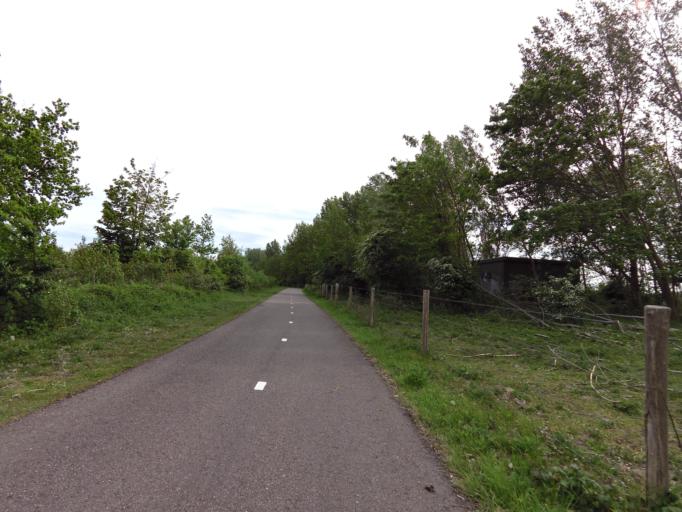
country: NL
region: South Holland
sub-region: Gemeente Rotterdam
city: Hoek van Holland
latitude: 51.9262
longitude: 4.1020
